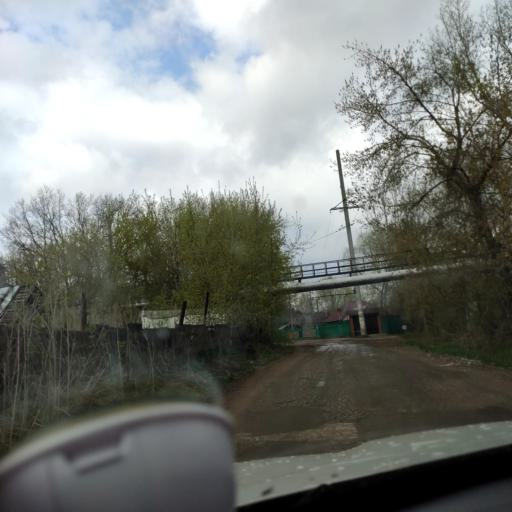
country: RU
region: Samara
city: Novokuybyshevsk
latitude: 53.1414
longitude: 49.9697
